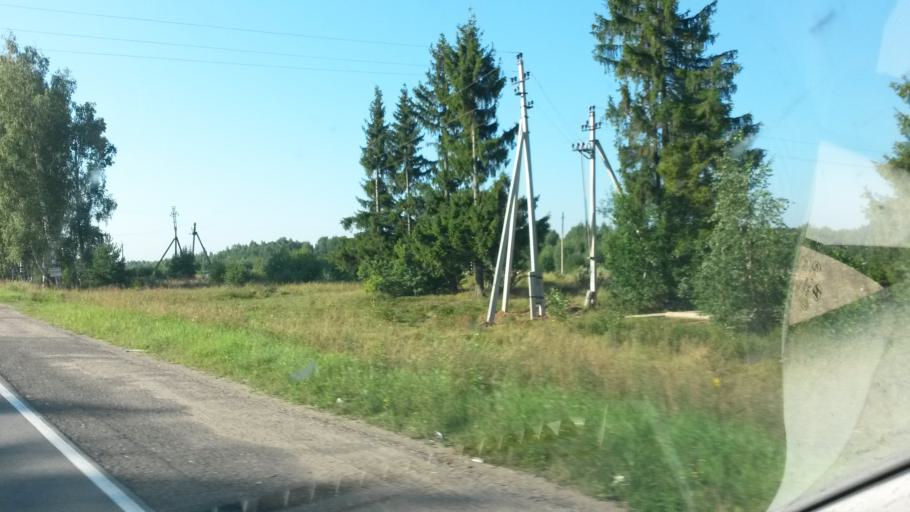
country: RU
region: Ivanovo
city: Pistsovo
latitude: 57.1554
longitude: 40.5657
